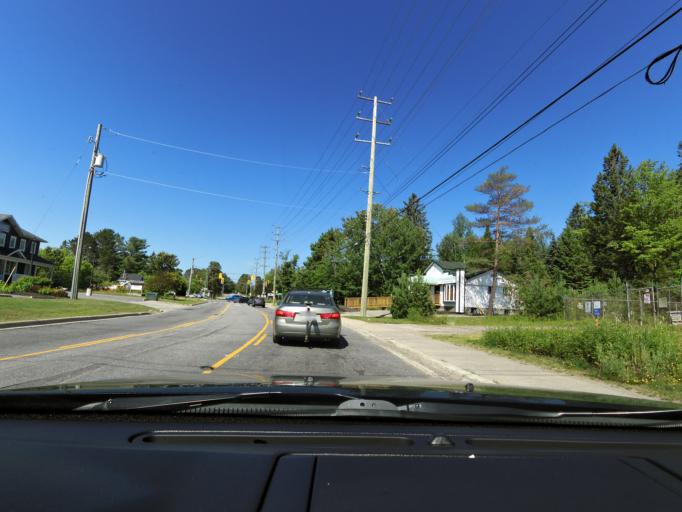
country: CA
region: Ontario
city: Huntsville
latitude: 45.3335
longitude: -79.2230
